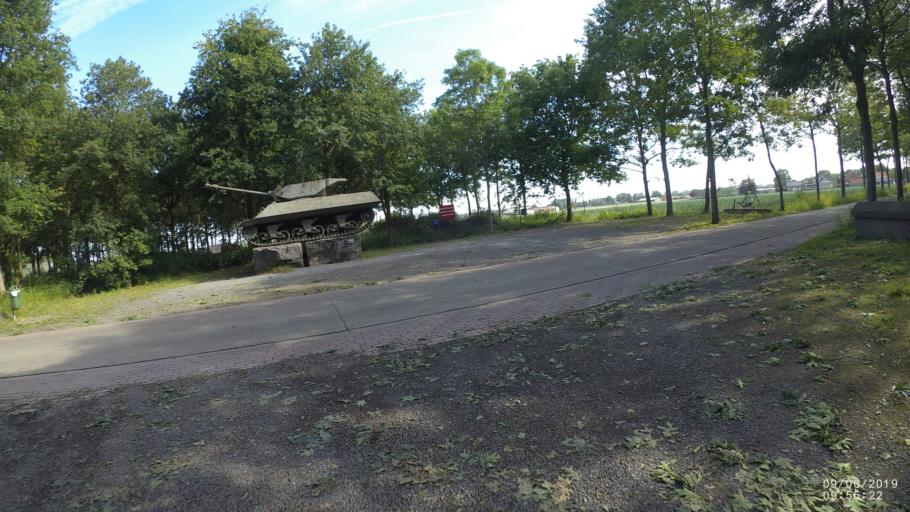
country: BE
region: Flanders
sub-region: Provincie Oost-Vlaanderen
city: Eeklo
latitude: 51.1901
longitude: 3.5013
